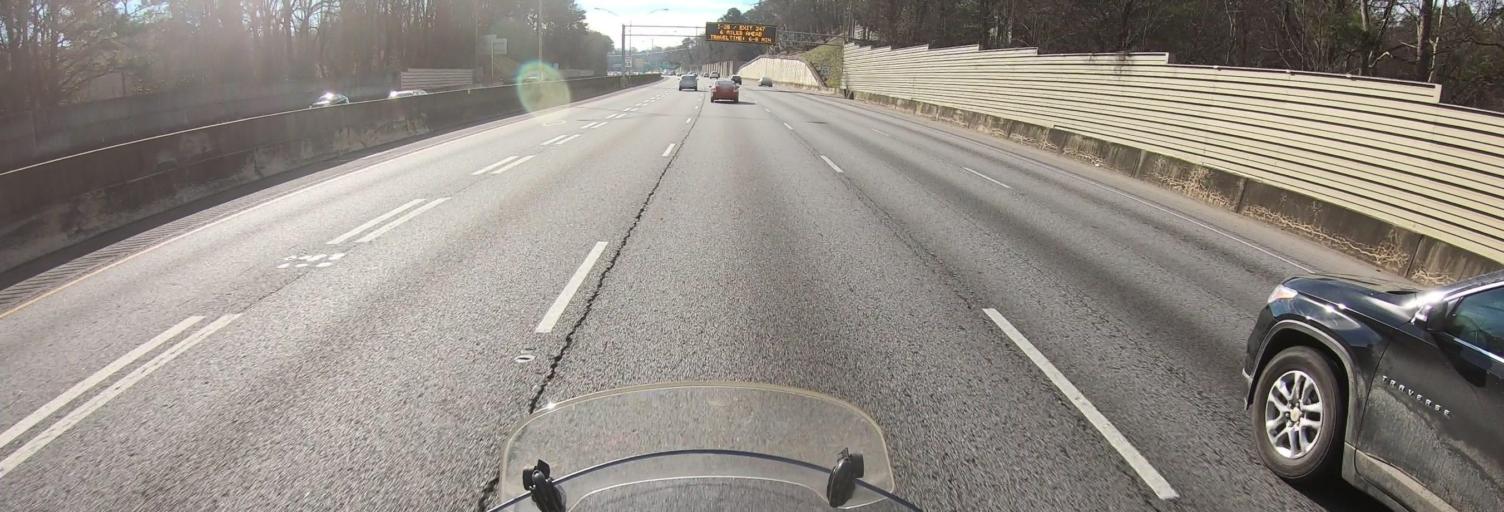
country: US
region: Georgia
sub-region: Fulton County
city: Atlanta
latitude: 33.8021
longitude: -84.4164
